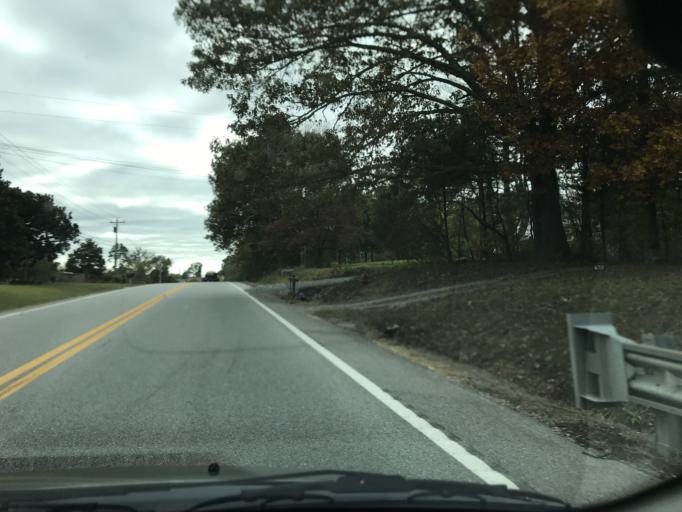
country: US
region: Tennessee
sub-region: Hamilton County
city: Lakesite
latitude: 35.2126
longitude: -85.0328
